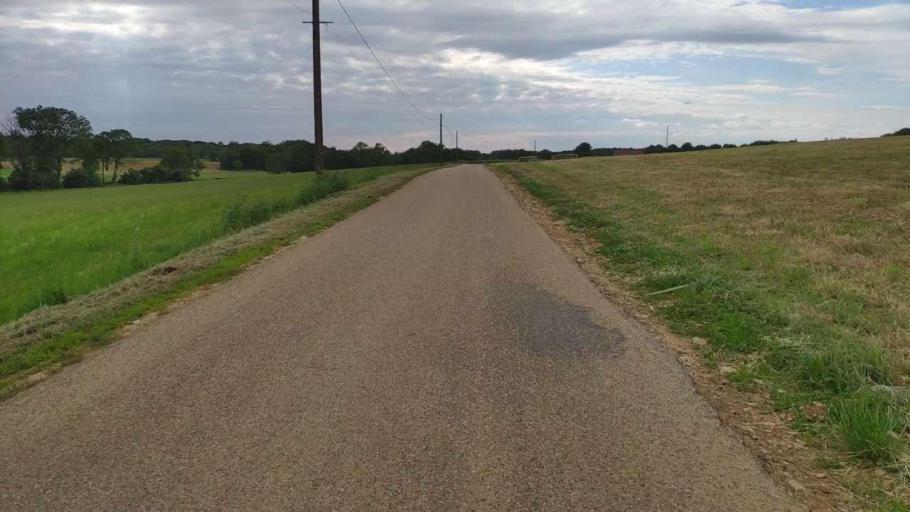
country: FR
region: Franche-Comte
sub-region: Departement du Jura
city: Bletterans
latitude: 46.7987
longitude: 5.5427
